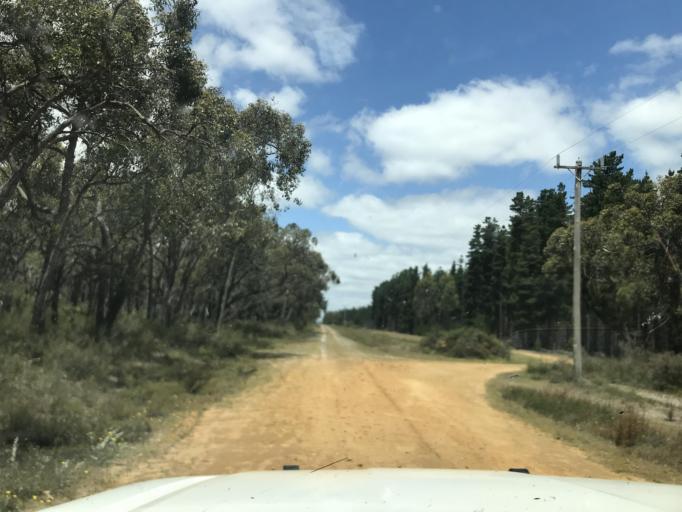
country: AU
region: South Australia
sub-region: Wattle Range
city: Penola
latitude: -37.3758
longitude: 141.1704
